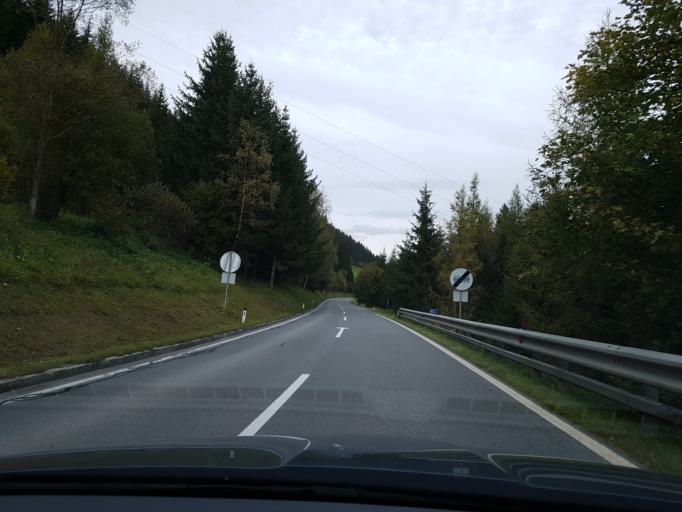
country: AT
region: Salzburg
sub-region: Politischer Bezirk Tamsweg
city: Tamsweg
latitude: 47.1077
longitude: 13.8169
